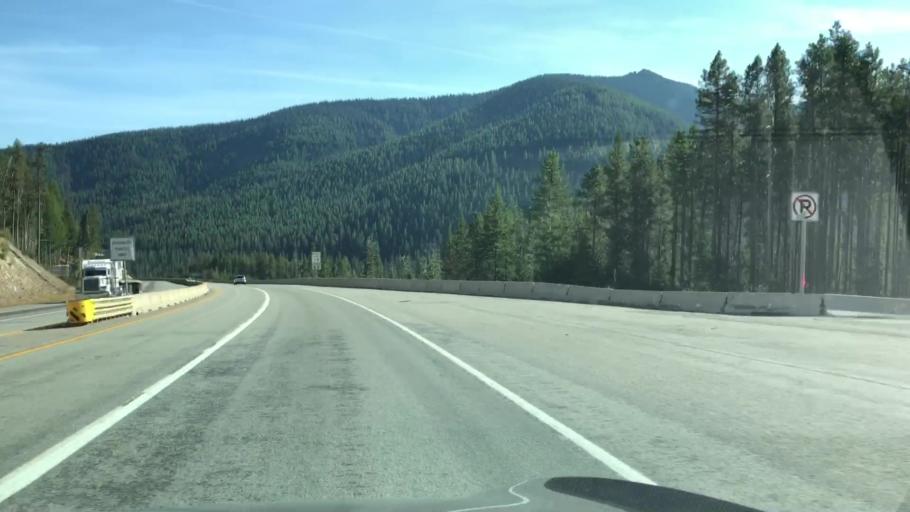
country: US
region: Idaho
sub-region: Shoshone County
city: Wallace
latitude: 47.4476
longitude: -115.6935
